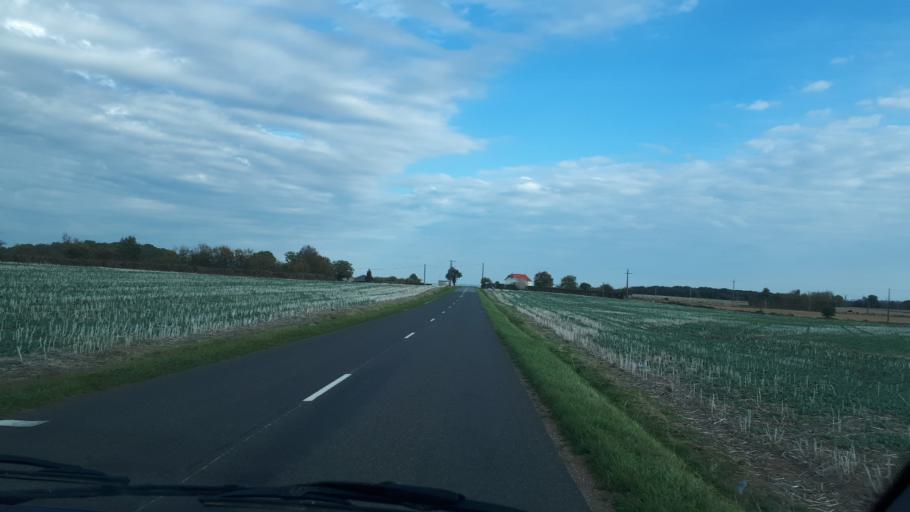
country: FR
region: Centre
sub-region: Departement du Loir-et-Cher
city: Mondoubleau
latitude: 47.9544
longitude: 0.9318
